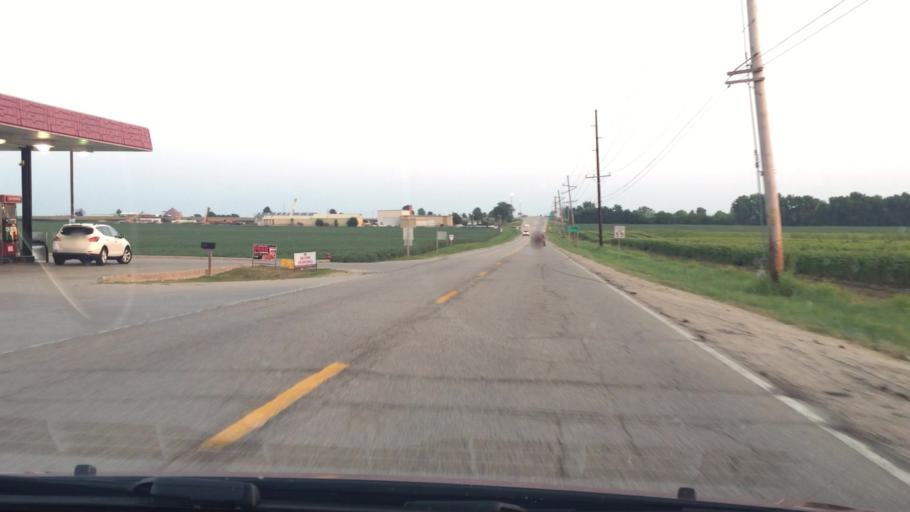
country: US
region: Illinois
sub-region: Bureau County
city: Ladd
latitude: 41.3775
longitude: -89.2190
